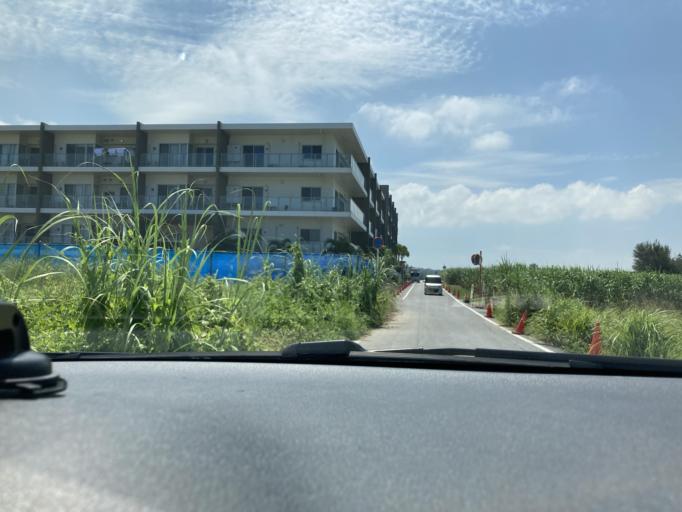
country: JP
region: Okinawa
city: Ishikawa
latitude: 26.4415
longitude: 127.7695
